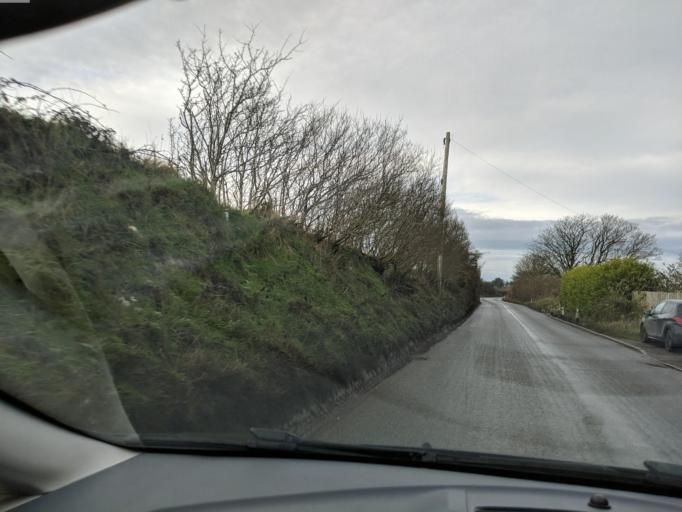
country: GB
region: England
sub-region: Cornwall
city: Jacobstow
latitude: 50.6705
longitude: -4.6021
